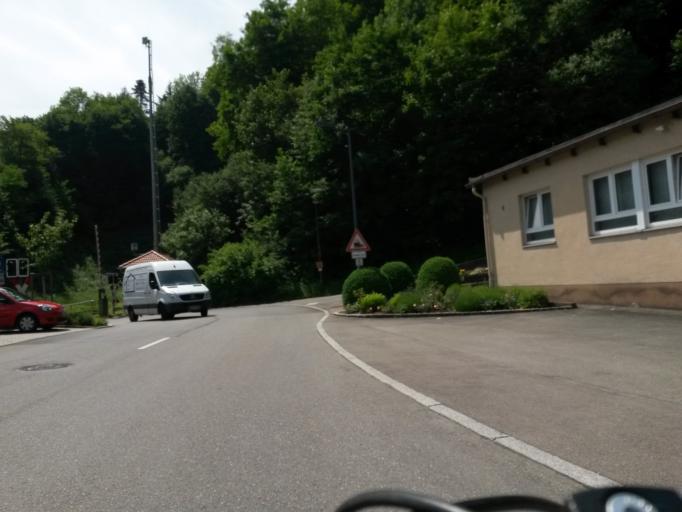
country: DE
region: Baden-Wuerttemberg
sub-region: Karlsruhe Region
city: Wildberg
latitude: 48.6251
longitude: 8.7427
